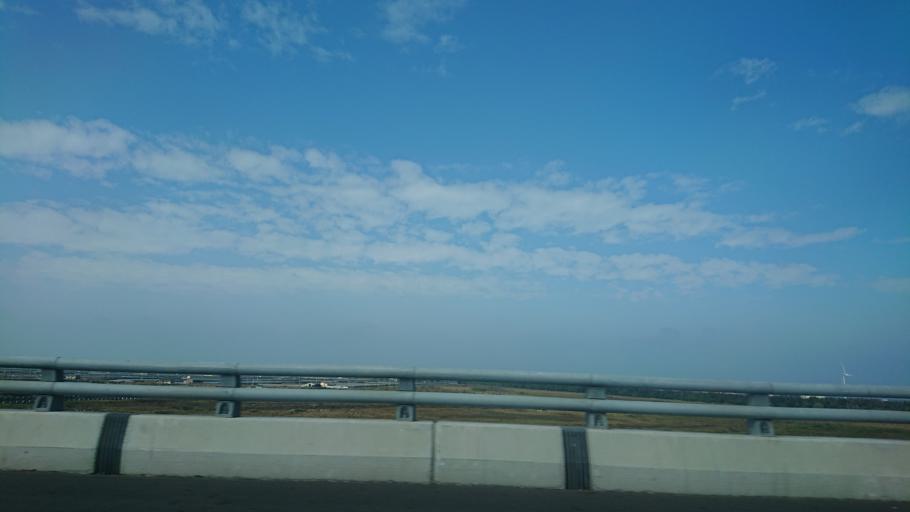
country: TW
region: Taiwan
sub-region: Changhua
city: Chang-hua
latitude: 23.9632
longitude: 120.3370
